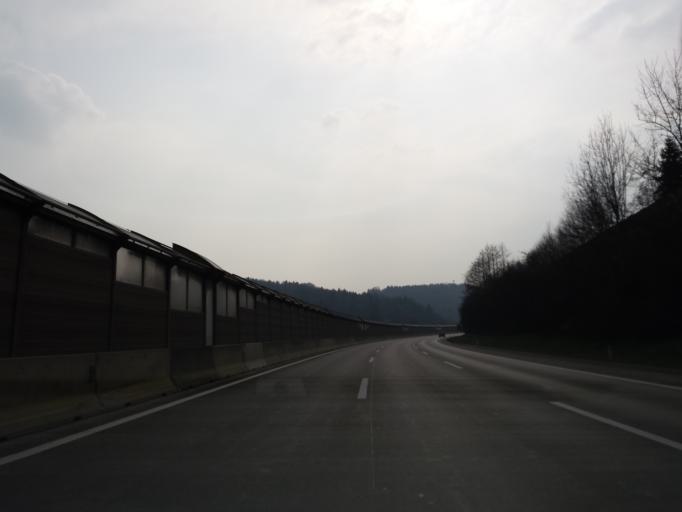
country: AT
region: Styria
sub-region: Politischer Bezirk Graz-Umgebung
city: Langegg bei Graz
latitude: 47.0730
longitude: 15.6394
